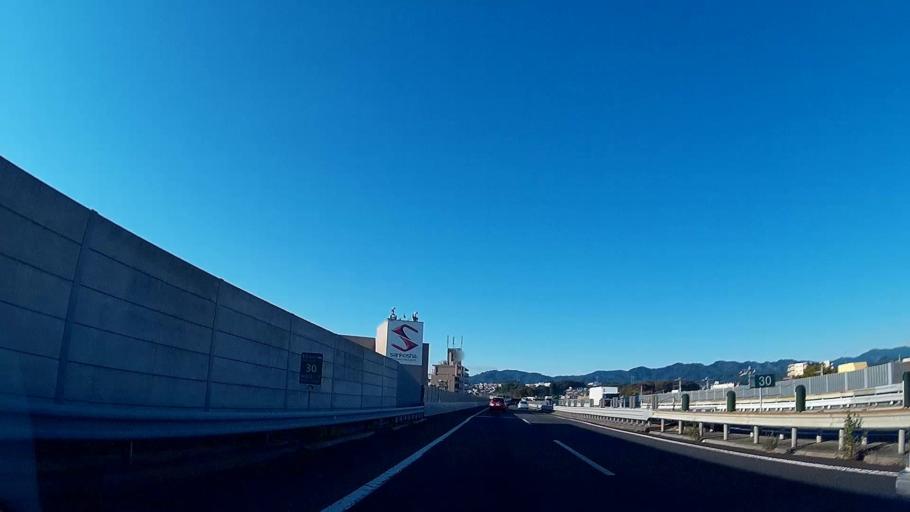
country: JP
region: Tokyo
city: Hachioji
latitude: 35.6705
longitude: 139.3058
